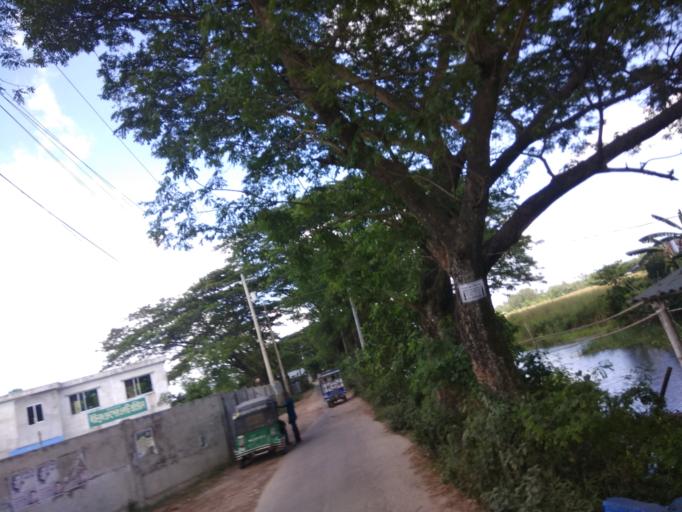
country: BD
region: Dhaka
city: Narayanganj
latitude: 23.4678
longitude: 90.4558
